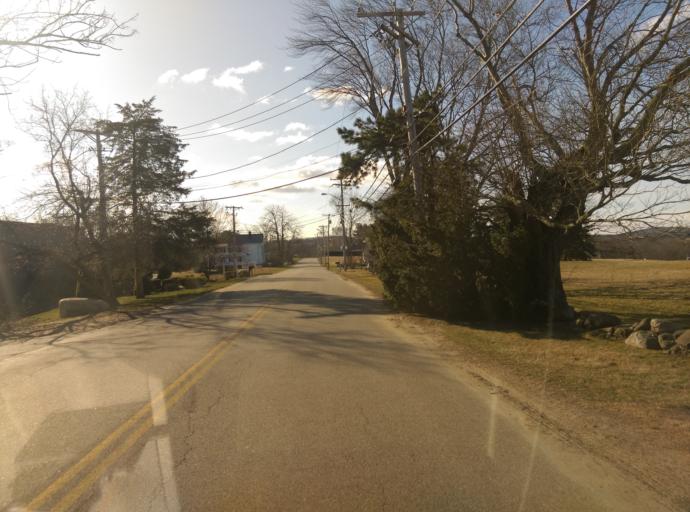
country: US
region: Massachusetts
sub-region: Essex County
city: Haverhill
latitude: 42.7530
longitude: -71.1163
